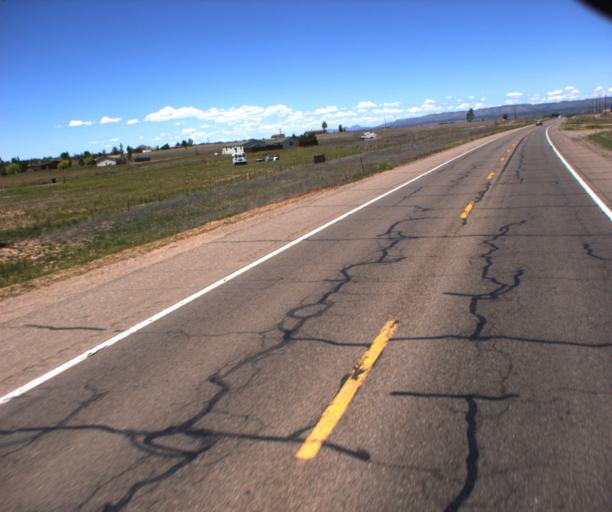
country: US
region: Arizona
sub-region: Yavapai County
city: Paulden
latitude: 34.8434
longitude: -112.4649
